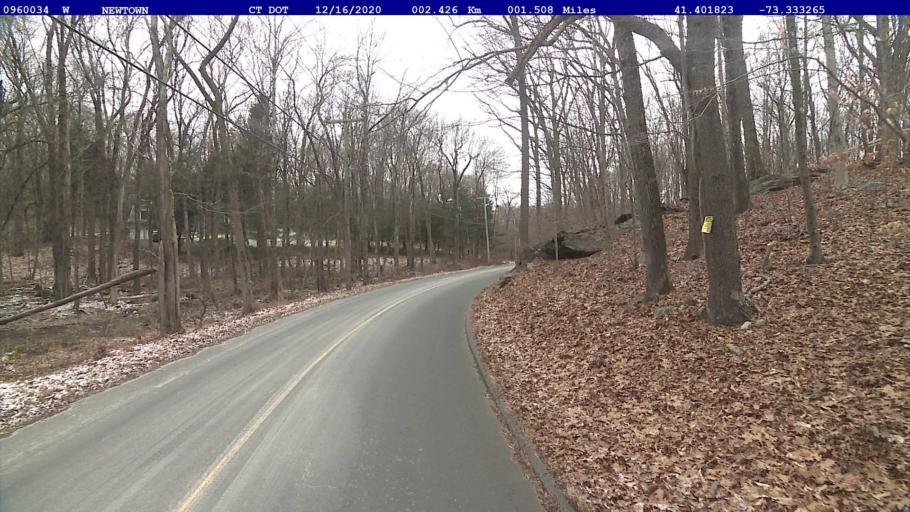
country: US
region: Connecticut
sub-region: Fairfield County
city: Newtown
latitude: 41.4018
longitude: -73.3333
